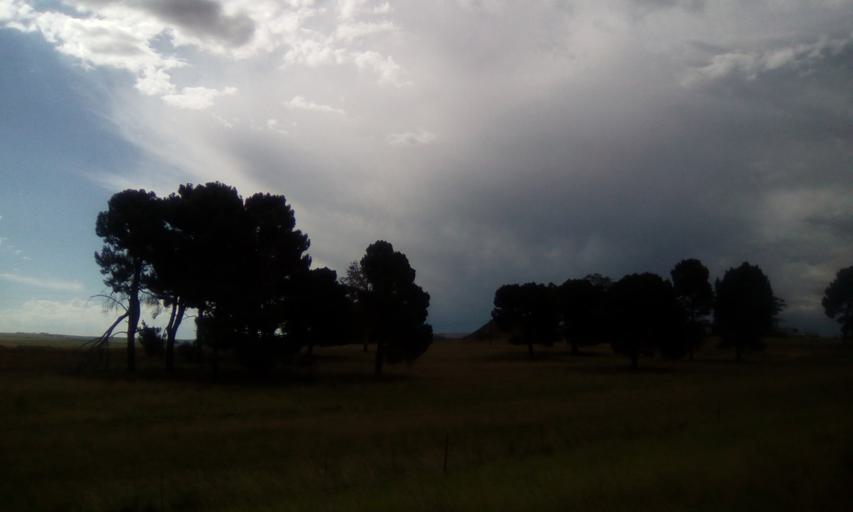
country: LS
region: Maseru
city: Maseru
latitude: -29.2649
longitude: 27.4339
